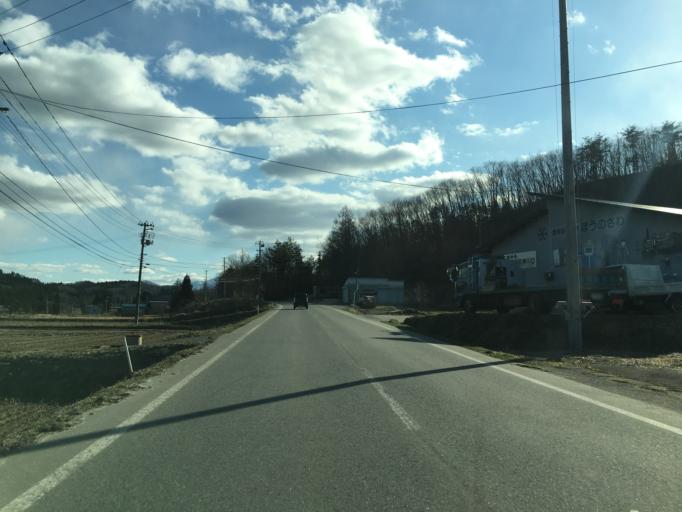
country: JP
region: Yamagata
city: Nagai
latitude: 37.9886
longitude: 140.0039
